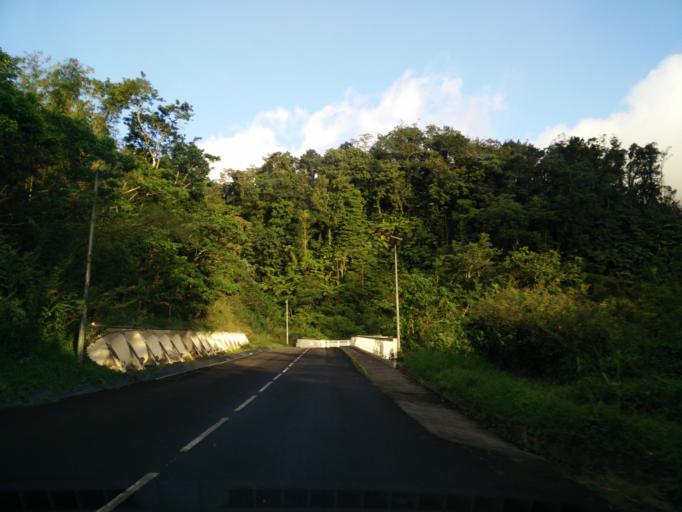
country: MQ
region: Martinique
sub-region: Martinique
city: Le Morne-Rouge
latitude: 14.7285
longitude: -61.1171
